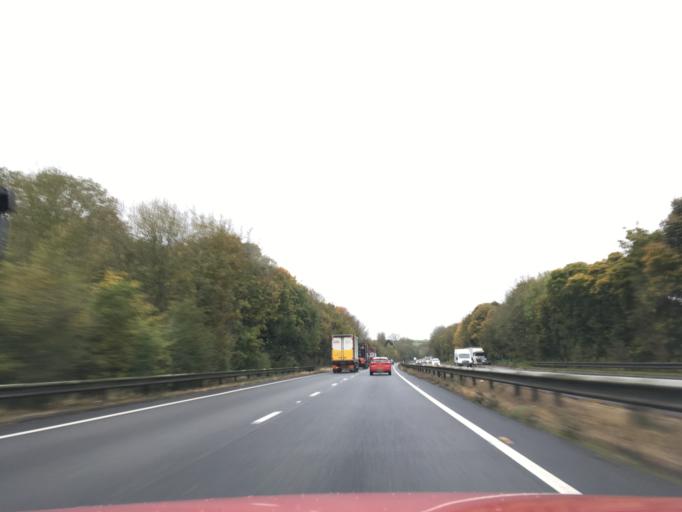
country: GB
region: England
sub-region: Hampshire
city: Overton
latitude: 51.2265
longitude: -1.3462
